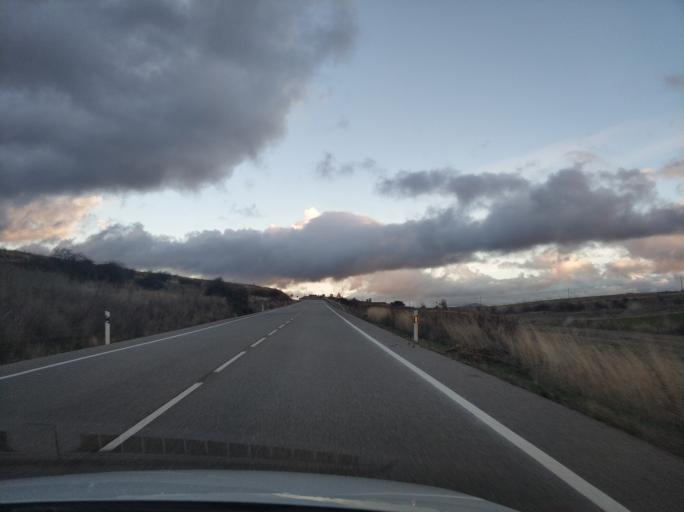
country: ES
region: Castille and Leon
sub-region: Provincia de Segovia
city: Ayllon
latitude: 41.4154
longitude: -3.4029
